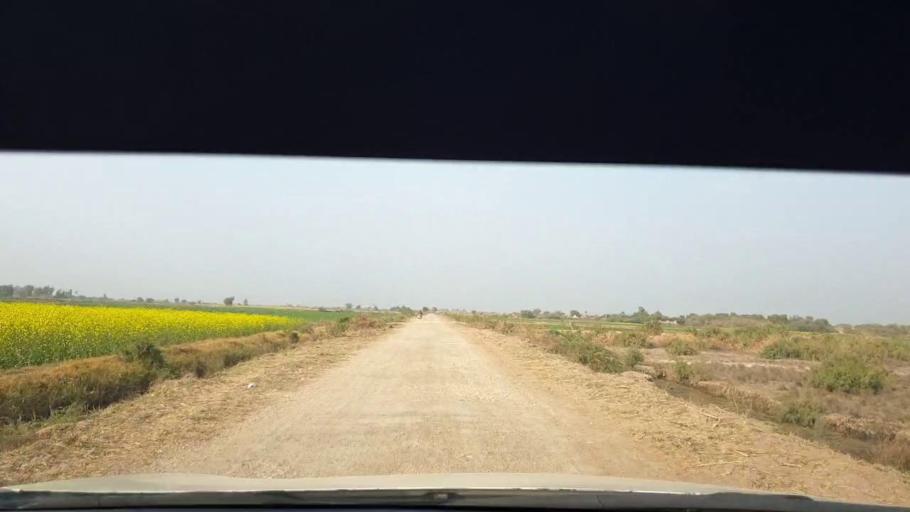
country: PK
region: Sindh
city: Berani
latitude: 25.7546
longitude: 68.9407
